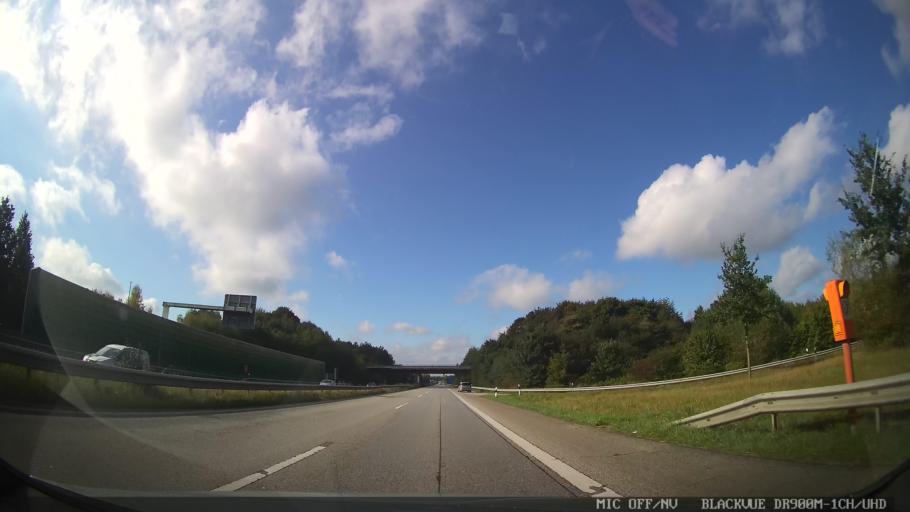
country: DE
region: Schleswig-Holstein
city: Oldenburg in Holstein
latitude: 54.3021
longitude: 10.8917
